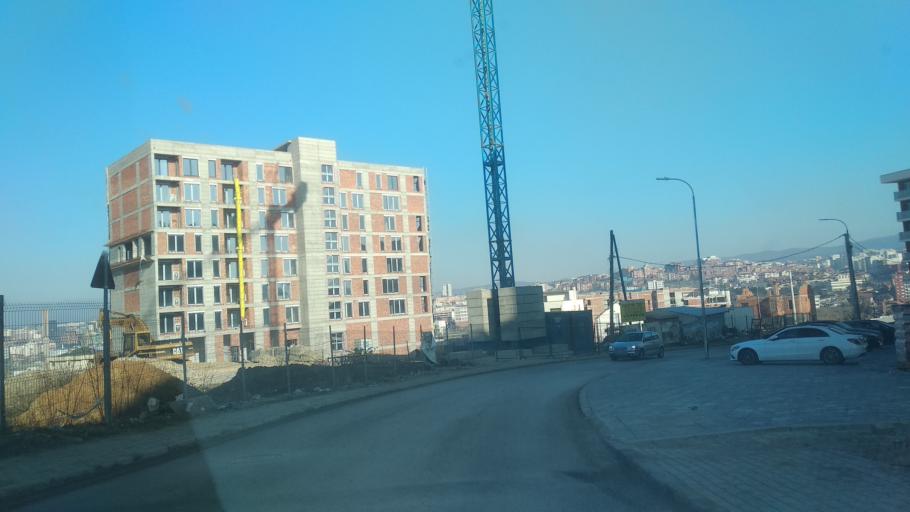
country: XK
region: Pristina
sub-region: Komuna e Prishtines
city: Pristina
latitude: 42.6378
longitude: 21.1596
